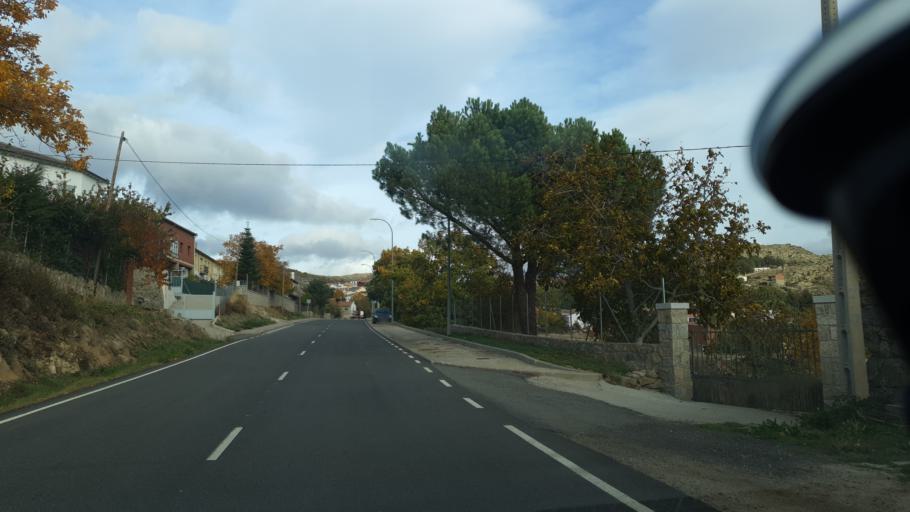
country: ES
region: Castille and Leon
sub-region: Provincia de Avila
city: Navalosa
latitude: 40.3989
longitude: -4.9353
